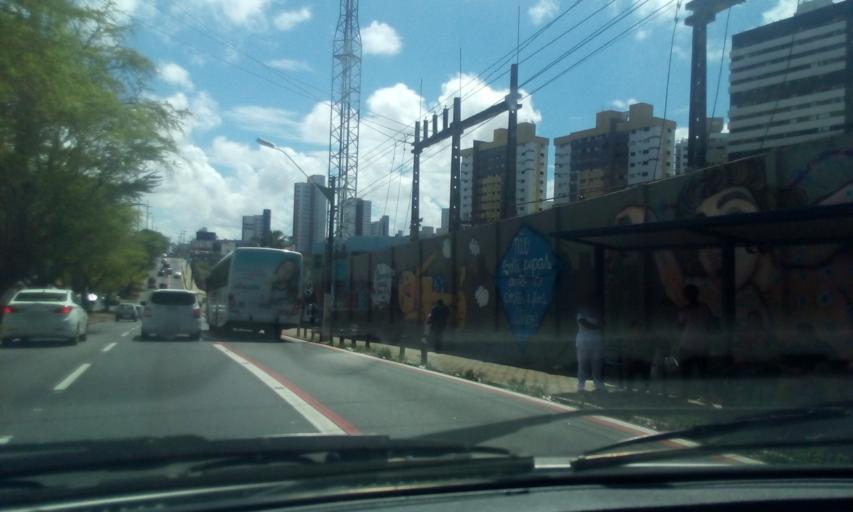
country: BR
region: Rio Grande do Norte
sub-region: Natal
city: Natal
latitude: -5.7945
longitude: -35.2038
